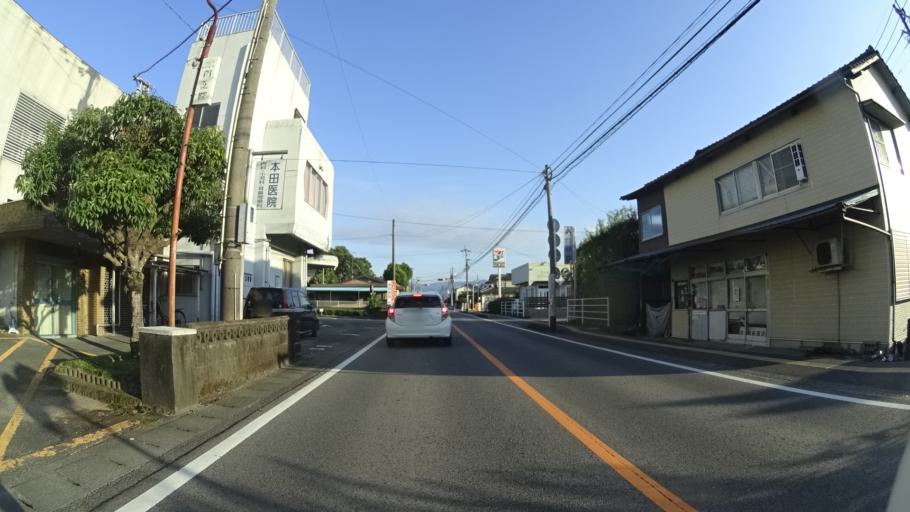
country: JP
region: Kumamoto
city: Matsubase
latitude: 32.6242
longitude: 130.6779
